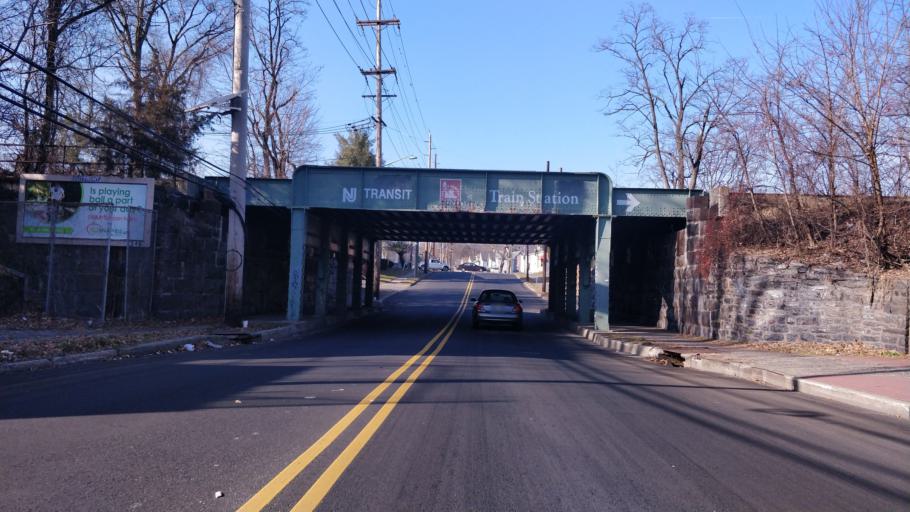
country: US
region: New Jersey
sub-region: Middlesex County
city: Dunellen
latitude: 40.6020
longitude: -74.4453
